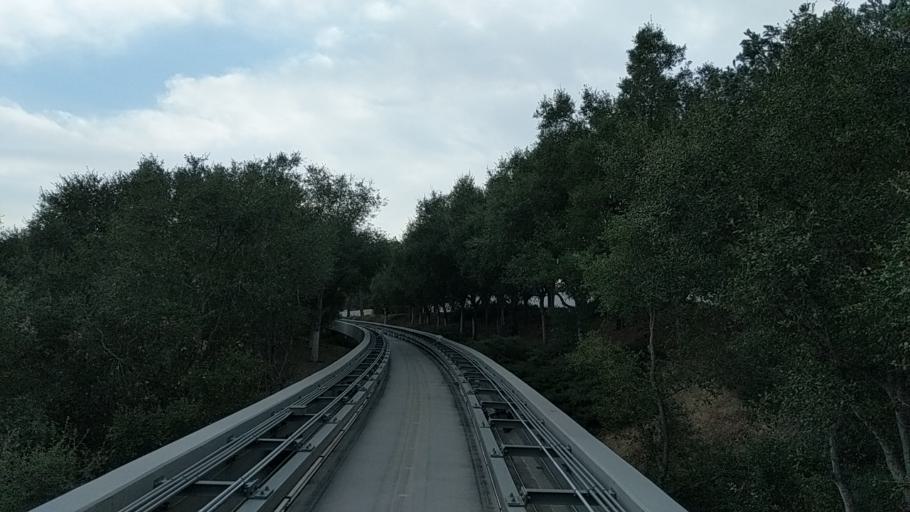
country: US
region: California
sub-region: Los Angeles County
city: Westwood, Los Angeles
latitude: 34.0819
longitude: -118.4755
